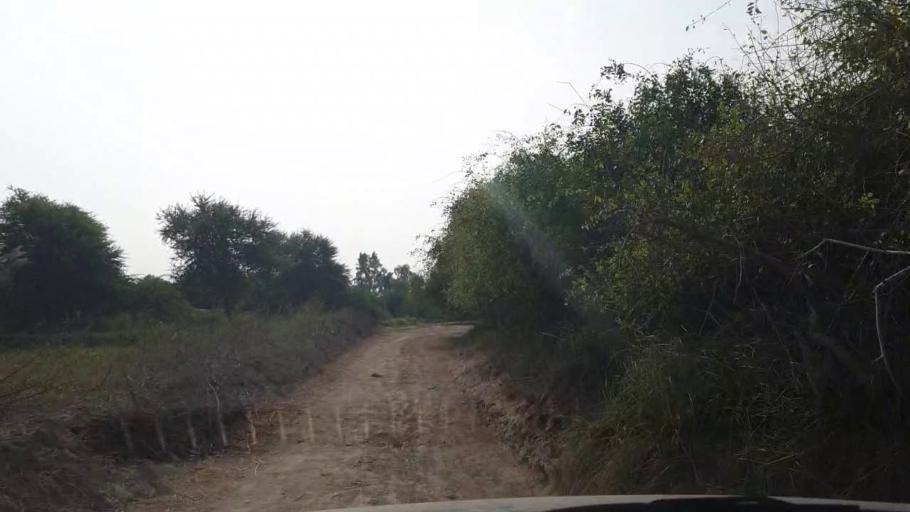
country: PK
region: Sindh
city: Rajo Khanani
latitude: 24.9056
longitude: 68.9212
